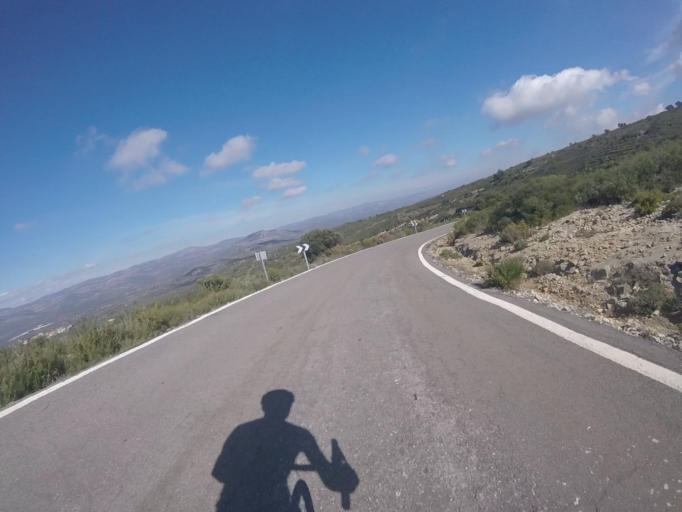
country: ES
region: Valencia
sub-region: Provincia de Castello
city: Albocasser
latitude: 40.3468
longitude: 0.0480
